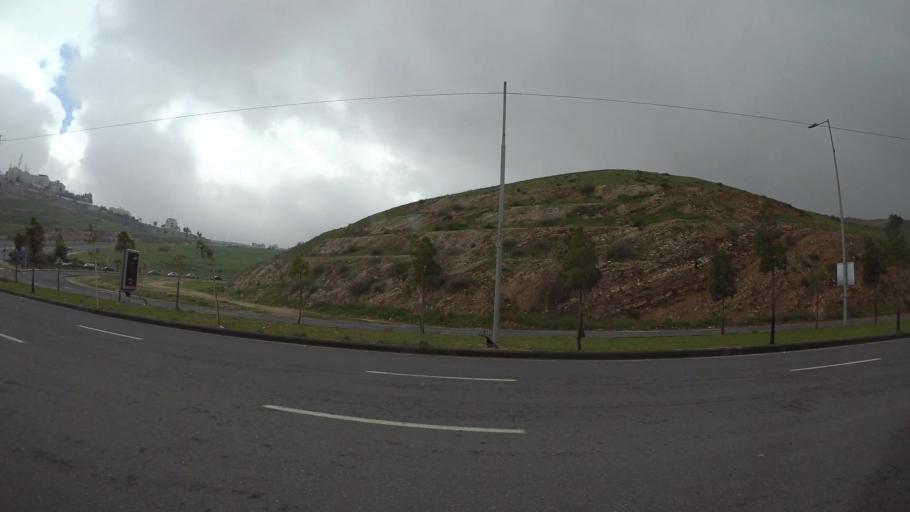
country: JO
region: Amman
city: Al Bunayyat ash Shamaliyah
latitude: 31.9298
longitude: 35.8786
